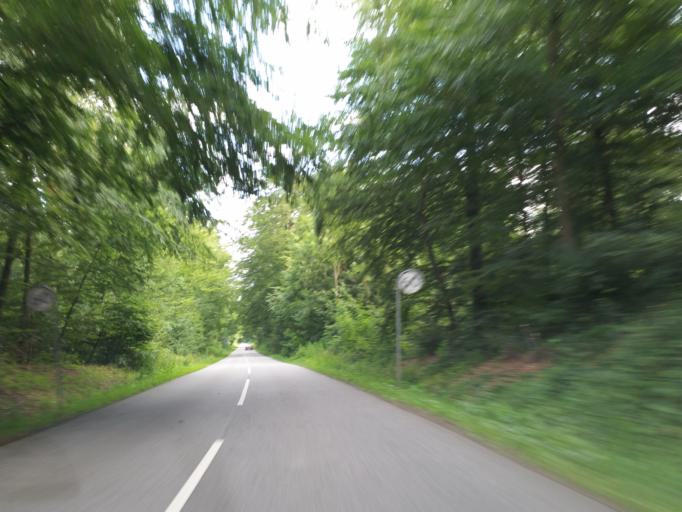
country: DK
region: South Denmark
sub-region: Vejle Kommune
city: Borkop
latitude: 55.6844
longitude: 9.6152
